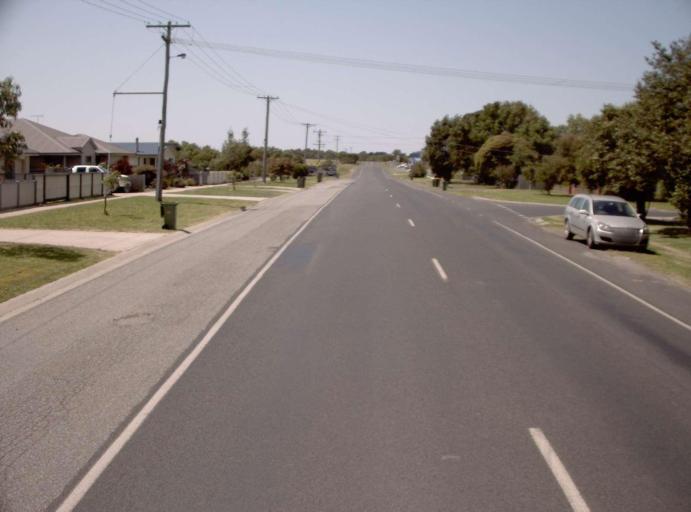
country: AU
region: Victoria
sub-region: Bass Coast
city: North Wonthaggi
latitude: -38.6159
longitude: 145.5976
